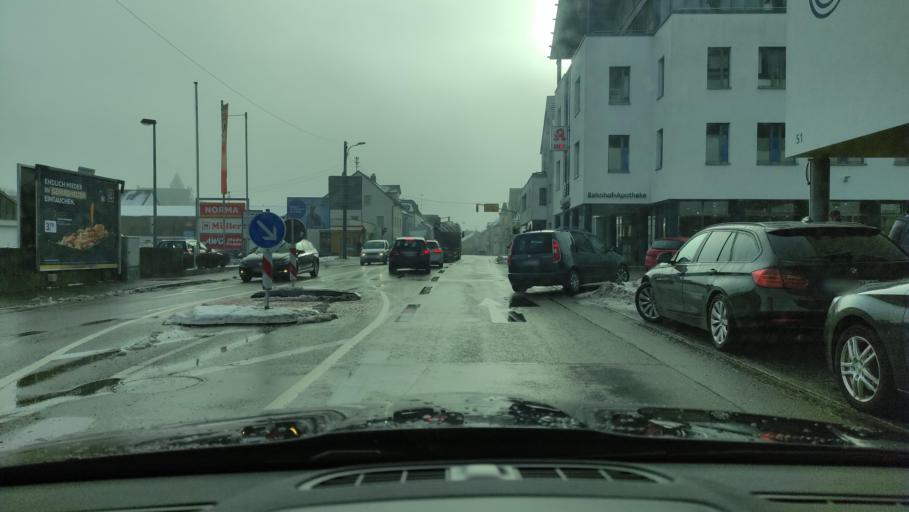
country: DE
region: Bavaria
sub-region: Swabia
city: Krumbach
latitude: 48.2473
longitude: 10.3594
